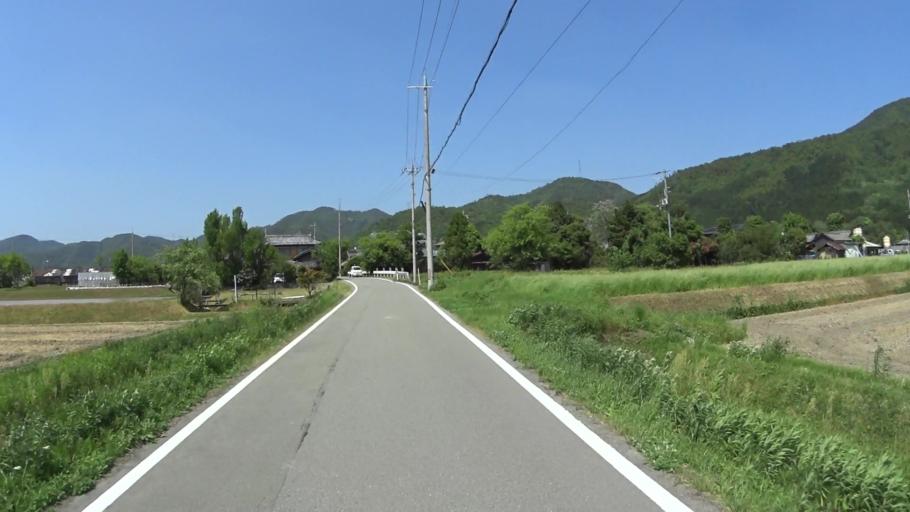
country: JP
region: Kyoto
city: Kameoka
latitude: 35.0745
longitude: 135.5630
